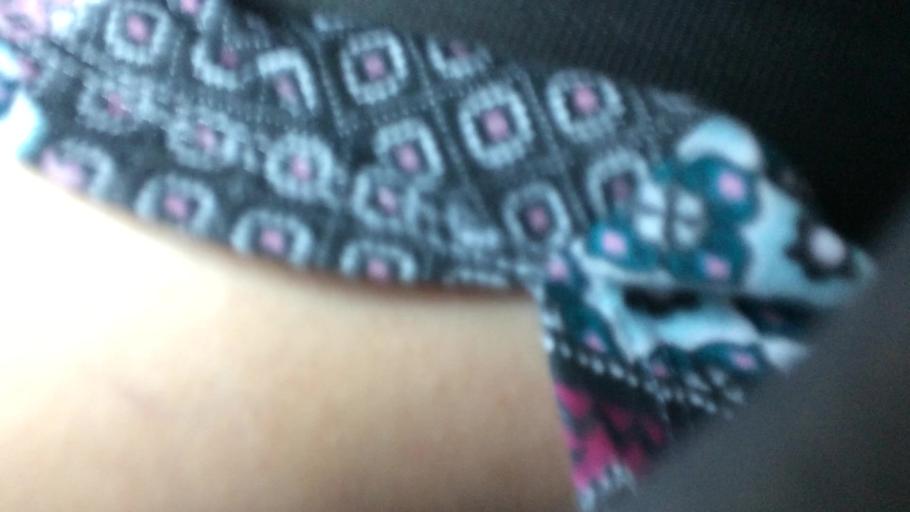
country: US
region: New Mexico
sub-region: Colfax County
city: Springer
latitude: 36.2094
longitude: -104.6621
